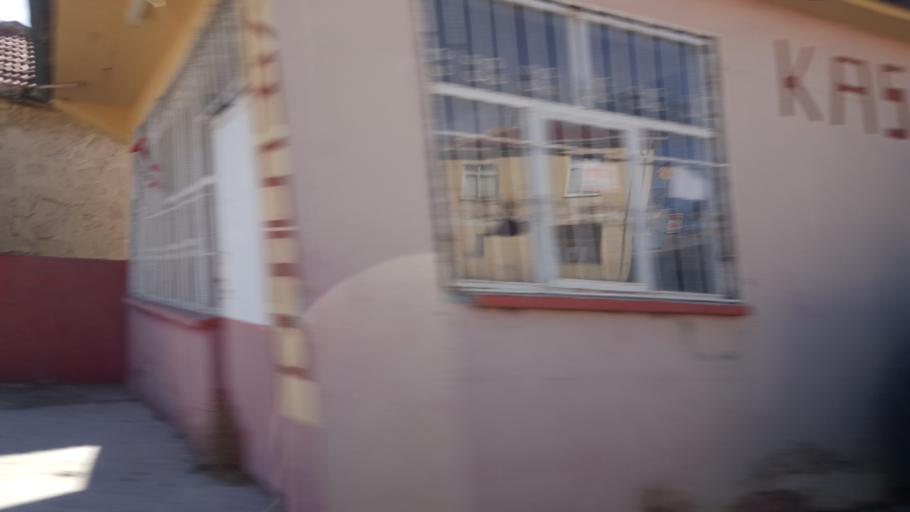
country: TR
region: Ankara
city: Yenice
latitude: 39.2739
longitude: 32.6801
